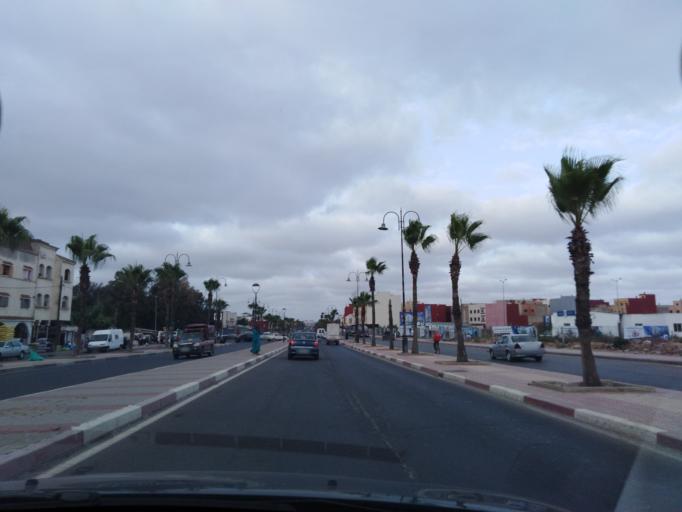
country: MA
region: Grand Casablanca
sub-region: Nouaceur
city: Dar Bouazza
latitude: 33.4153
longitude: -7.8644
